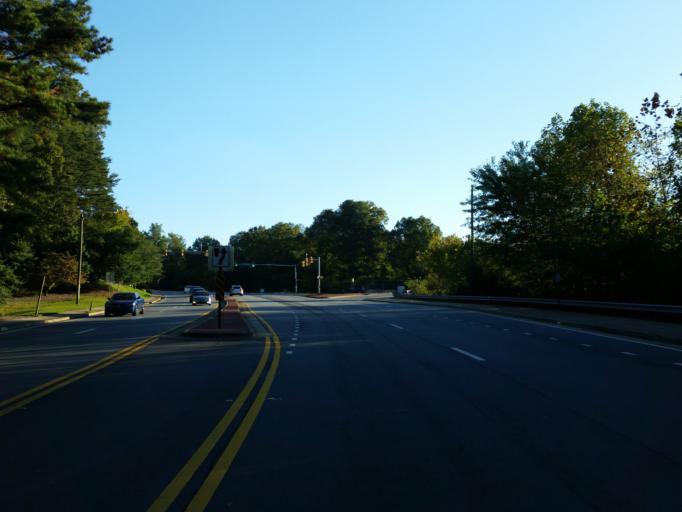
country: US
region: Georgia
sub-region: Cobb County
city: Vinings
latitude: 33.8737
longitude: -84.4746
